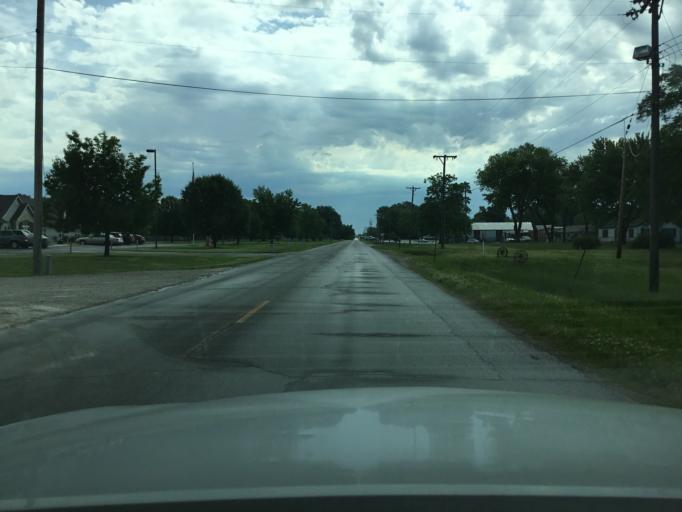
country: US
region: Kansas
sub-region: Montgomery County
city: Coffeyville
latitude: 37.0364
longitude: -95.6597
